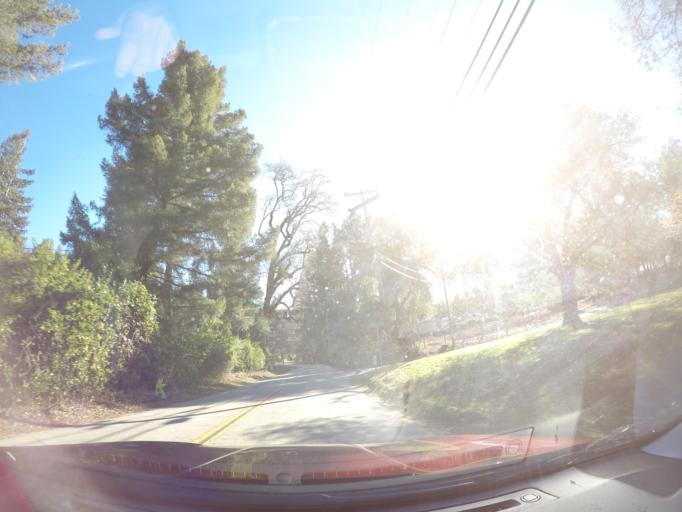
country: US
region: California
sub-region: Santa Cruz County
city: Scotts Valley
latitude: 37.0580
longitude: -122.0333
